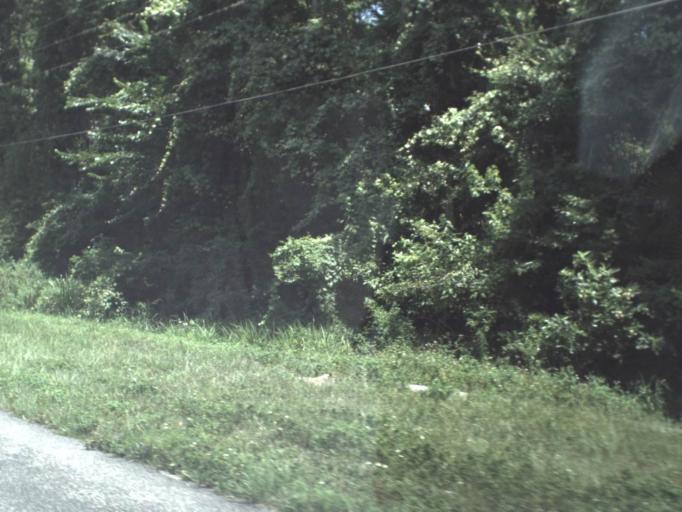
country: US
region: Florida
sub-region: Putnam County
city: Crescent City
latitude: 29.4588
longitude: -81.5201
